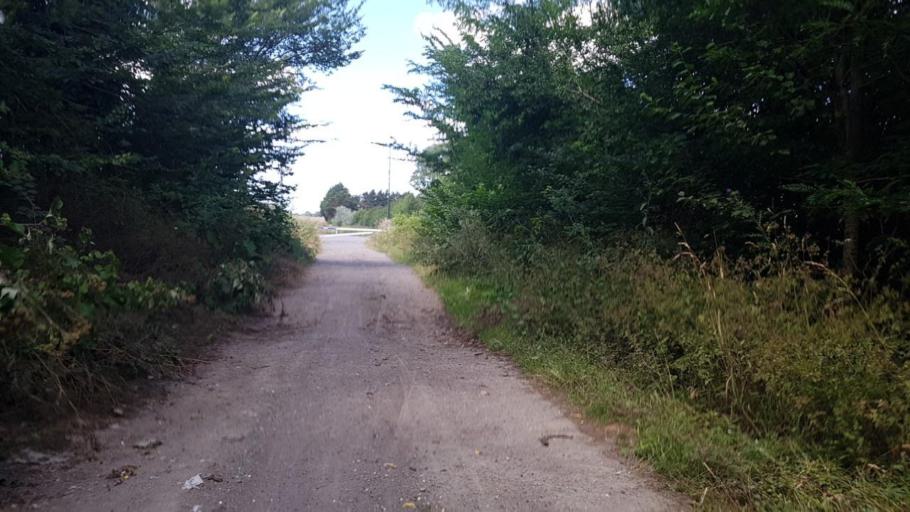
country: FR
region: Ile-de-France
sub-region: Departement de Seine-et-Marne
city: Claye-Souilly
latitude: 48.9761
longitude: 2.6691
